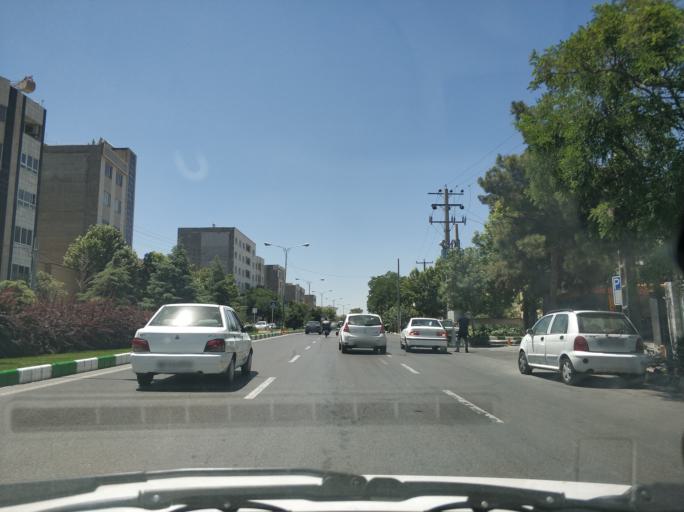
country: IR
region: Razavi Khorasan
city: Mashhad
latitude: 36.3122
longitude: 59.4947
